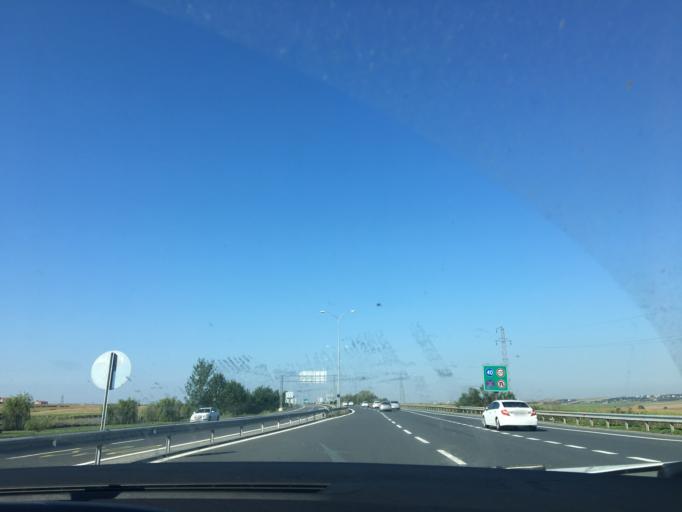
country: TR
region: Istanbul
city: Canta
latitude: 41.1112
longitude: 28.1662
